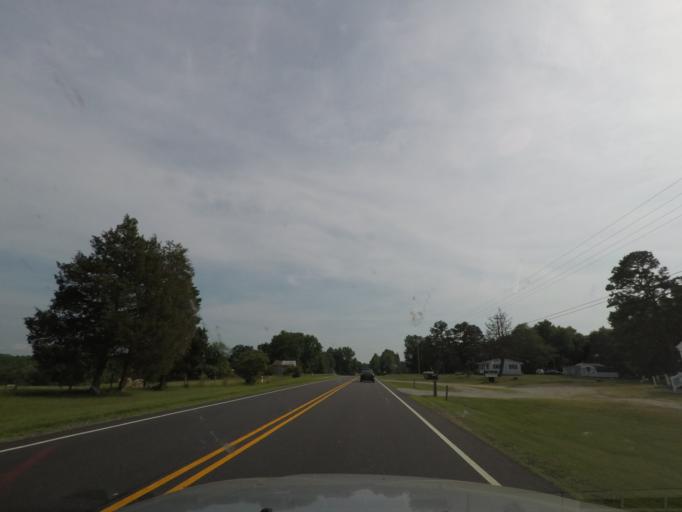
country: US
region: Virginia
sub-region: Prince Edward County
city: Hampden Sydney
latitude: 37.1305
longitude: -78.4494
